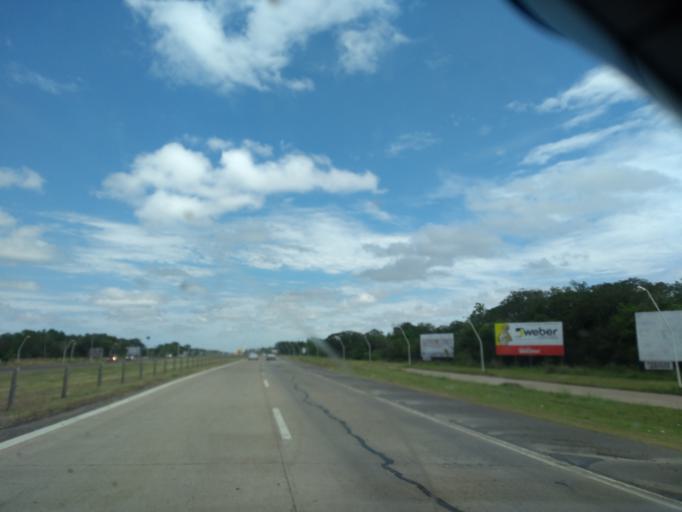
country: AR
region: Chaco
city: Barranqueras
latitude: -27.4346
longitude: -58.9225
